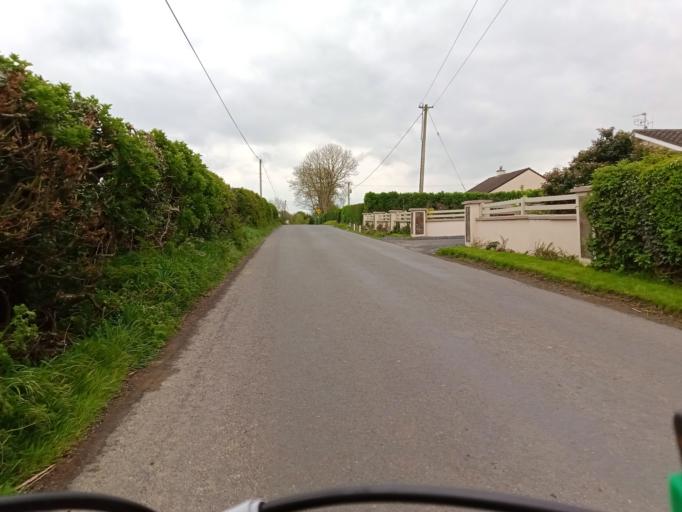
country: IE
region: Leinster
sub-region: Kilkenny
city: Kilkenny
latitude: 52.6191
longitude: -7.2662
